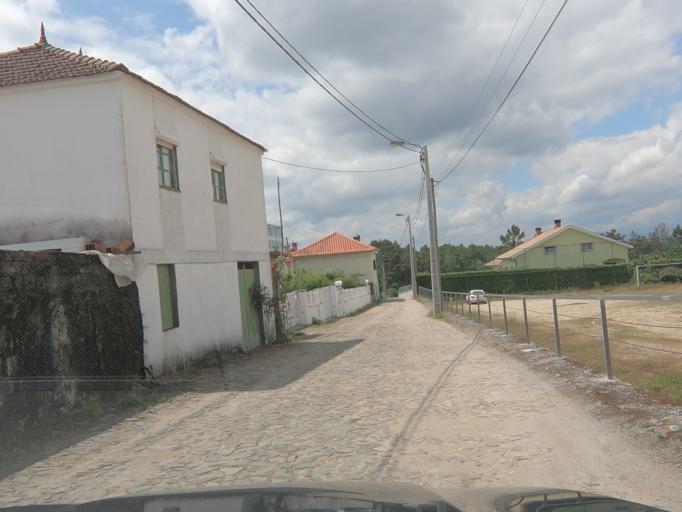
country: PT
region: Vila Real
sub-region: Sabrosa
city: Vilela
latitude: 41.2692
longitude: -7.6647
